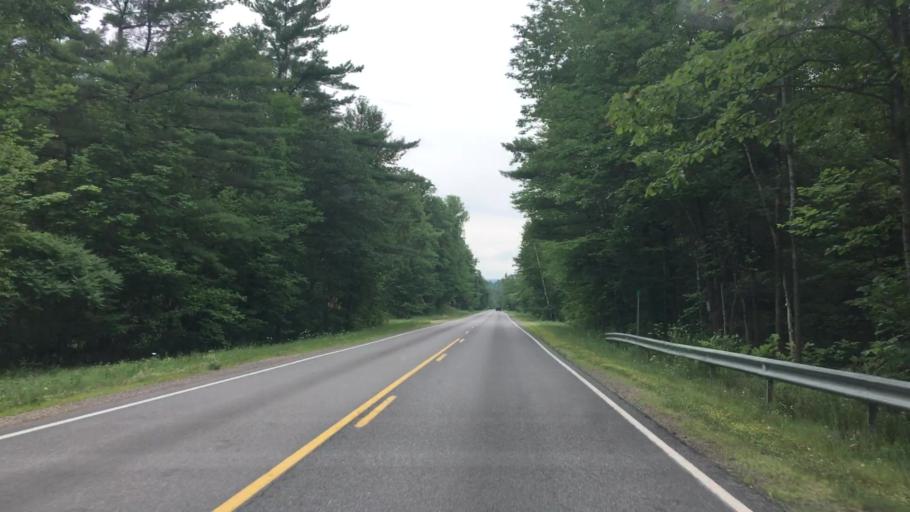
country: US
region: New York
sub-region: Clinton County
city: Peru
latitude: 44.4866
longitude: -73.5956
